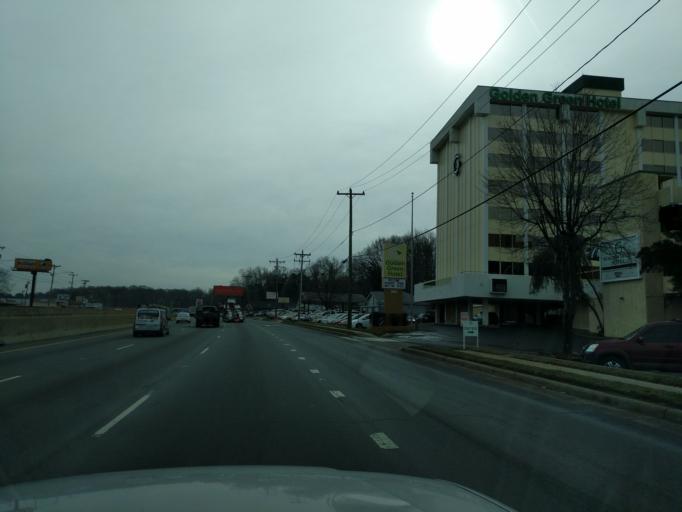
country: US
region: North Carolina
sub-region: Mecklenburg County
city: Charlotte
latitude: 35.2044
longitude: -80.7932
